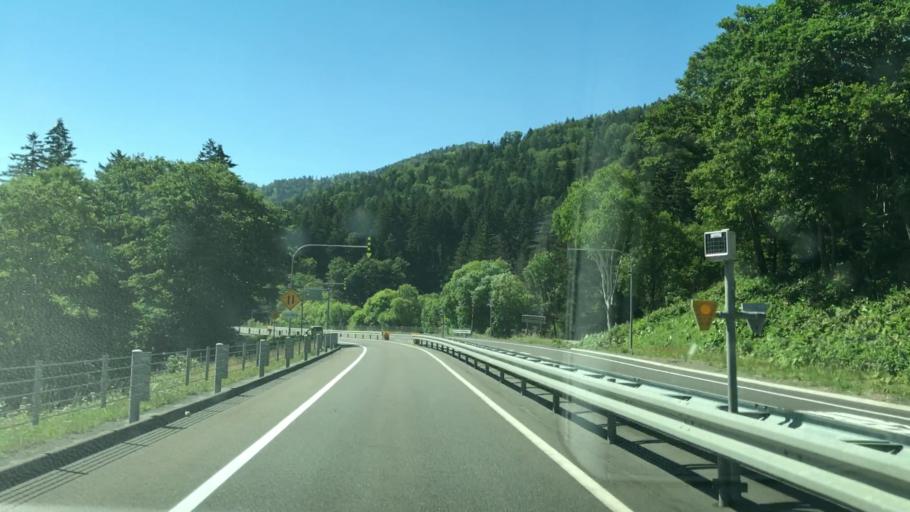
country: JP
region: Hokkaido
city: Otofuke
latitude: 42.9782
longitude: 142.7134
